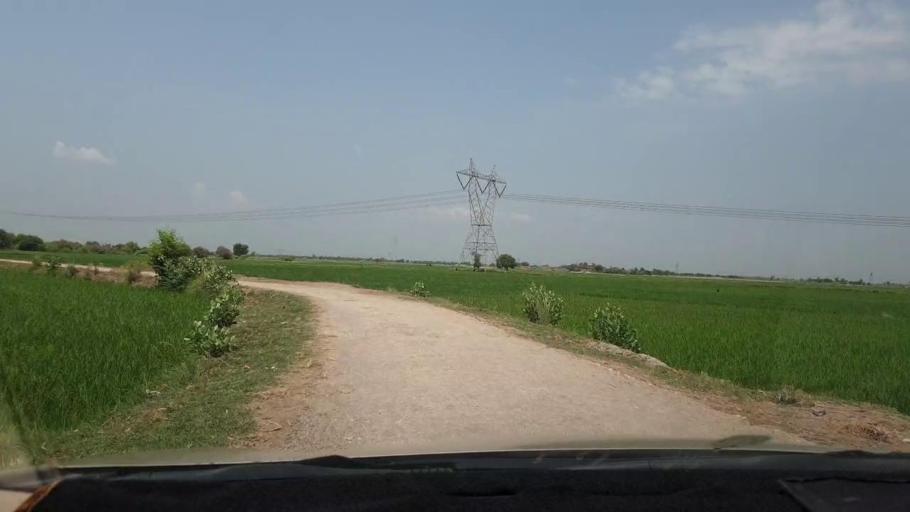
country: PK
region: Sindh
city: Naudero
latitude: 27.6642
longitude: 68.3063
